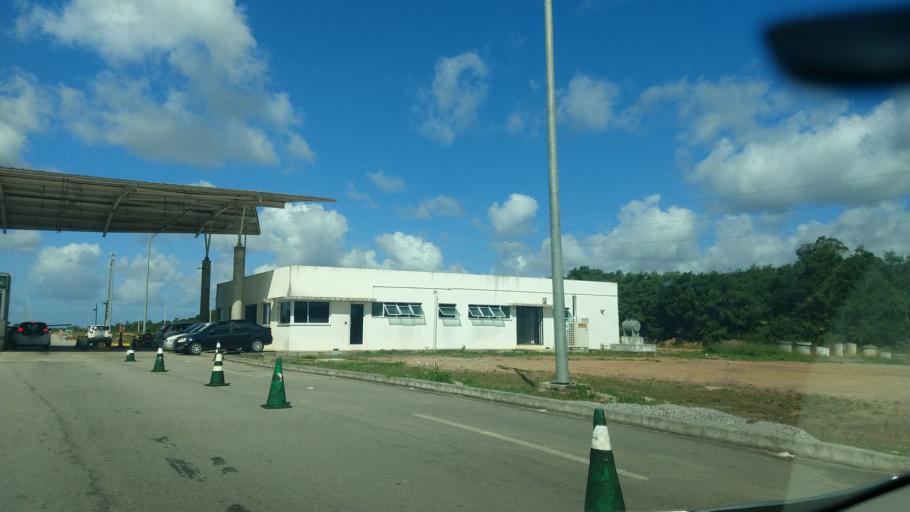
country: BR
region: Rio Grande do Norte
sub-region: Sao Goncalo Do Amarante
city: Sao Goncalo do Amarante
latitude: -5.7610
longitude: -35.3608
